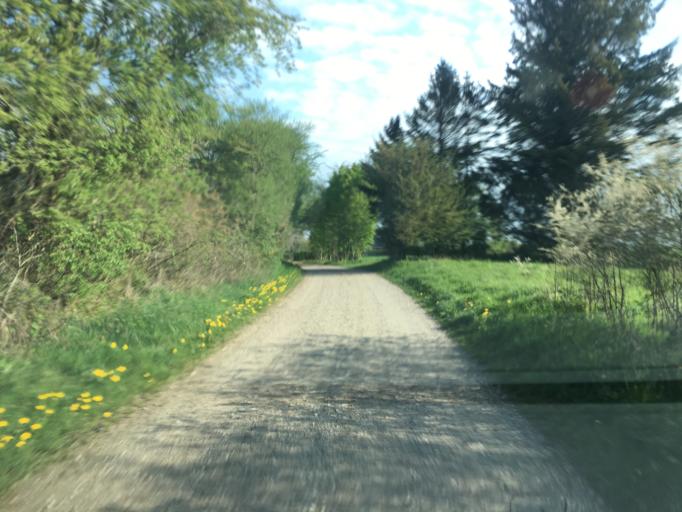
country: DK
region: South Denmark
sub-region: Haderslev Kommune
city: Vojens
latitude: 55.1767
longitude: 9.3865
